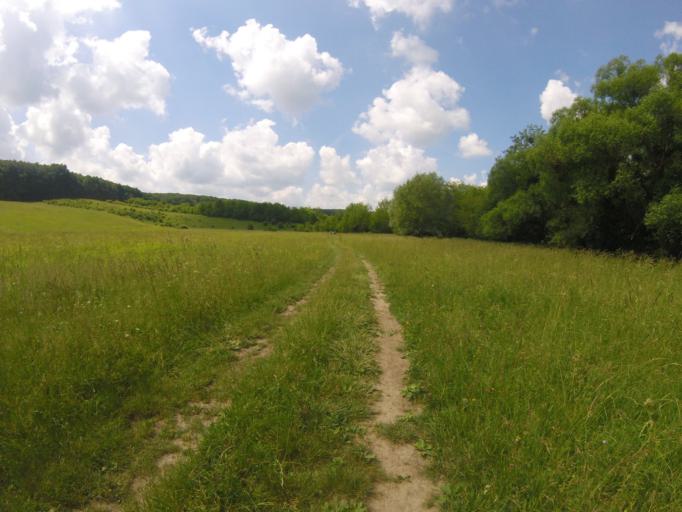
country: HU
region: Veszprem
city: Cseteny
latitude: 47.2757
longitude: 18.0112
